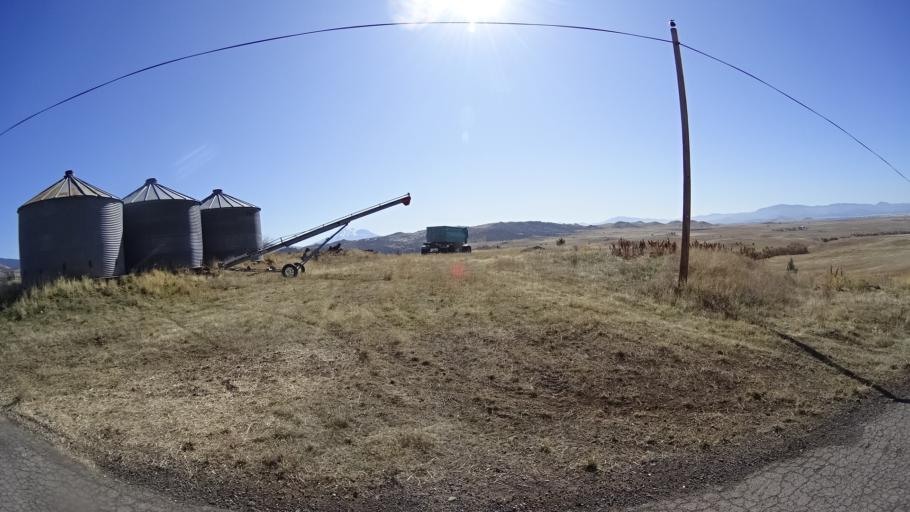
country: US
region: California
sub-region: Siskiyou County
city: Montague
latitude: 41.8310
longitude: -122.3927
